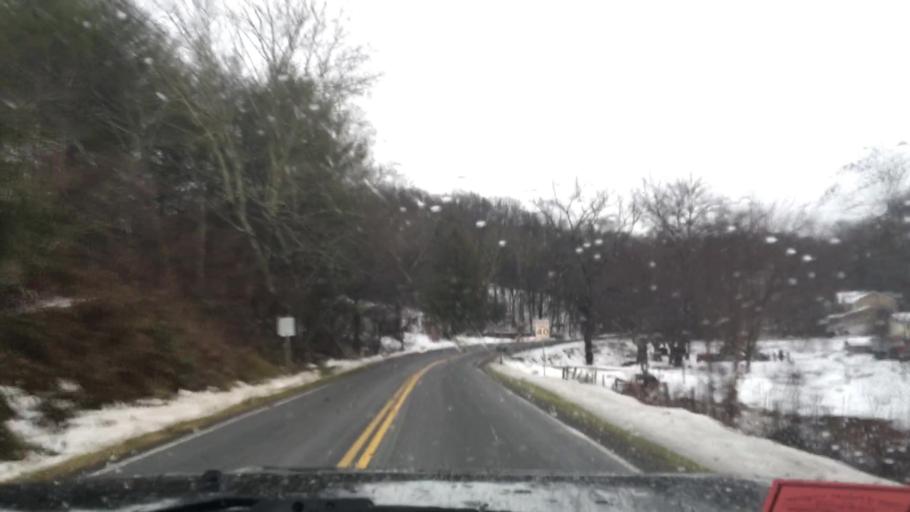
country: US
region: Virginia
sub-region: Pulaski County
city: Dublin
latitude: 37.0107
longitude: -80.6903
